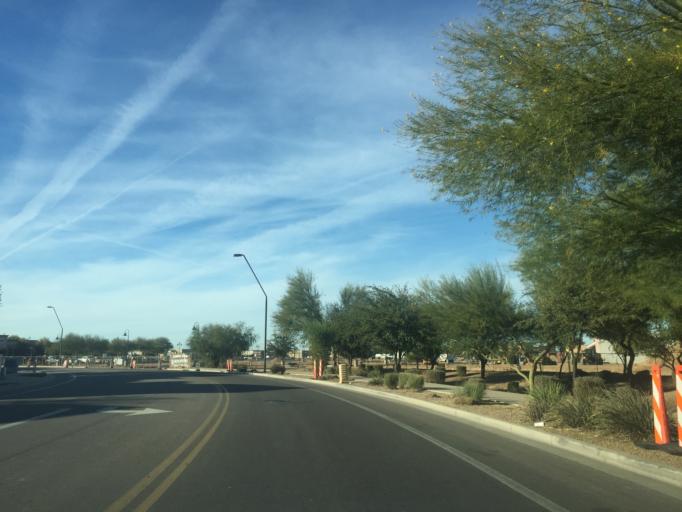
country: US
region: Arizona
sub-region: Maricopa County
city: Queen Creek
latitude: 33.2513
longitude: -111.6321
